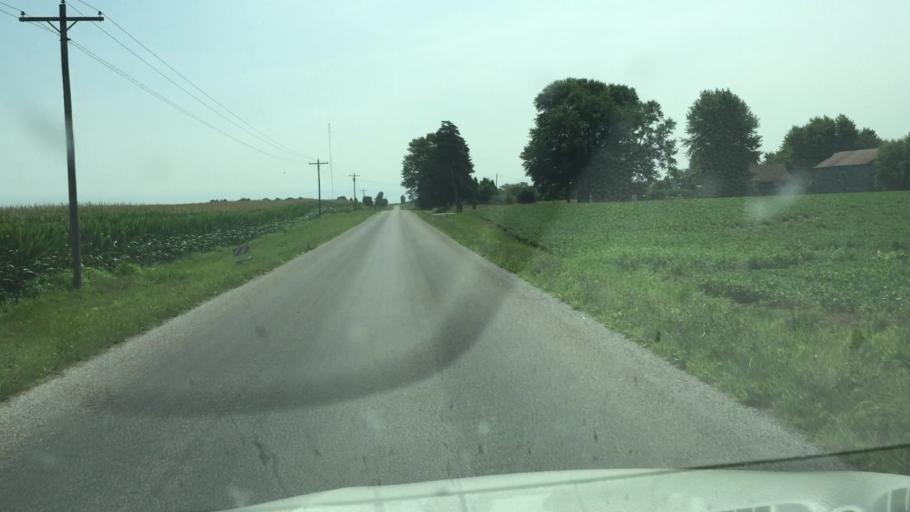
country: US
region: Illinois
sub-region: Hancock County
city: Nauvoo
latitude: 40.5113
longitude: -91.3389
